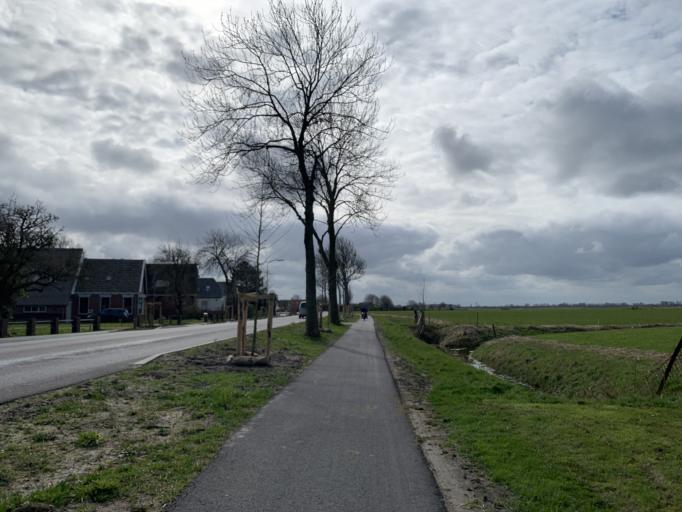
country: NL
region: Groningen
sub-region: Gemeente Groningen
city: Korrewegwijk
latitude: 53.2728
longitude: 6.5362
